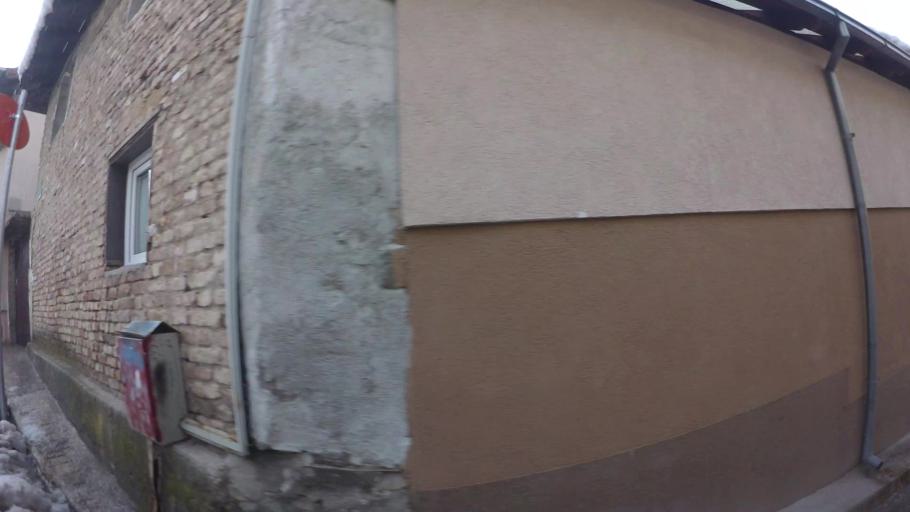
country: BA
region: Federation of Bosnia and Herzegovina
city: Kobilja Glava
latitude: 43.8652
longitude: 18.4360
